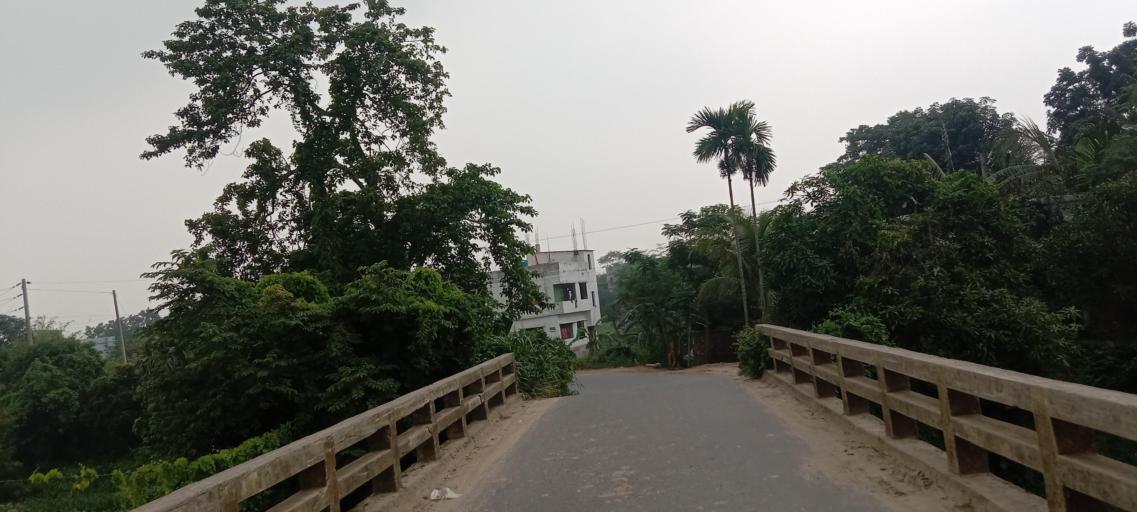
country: BD
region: Dhaka
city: Azimpur
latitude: 23.7398
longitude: 90.3151
